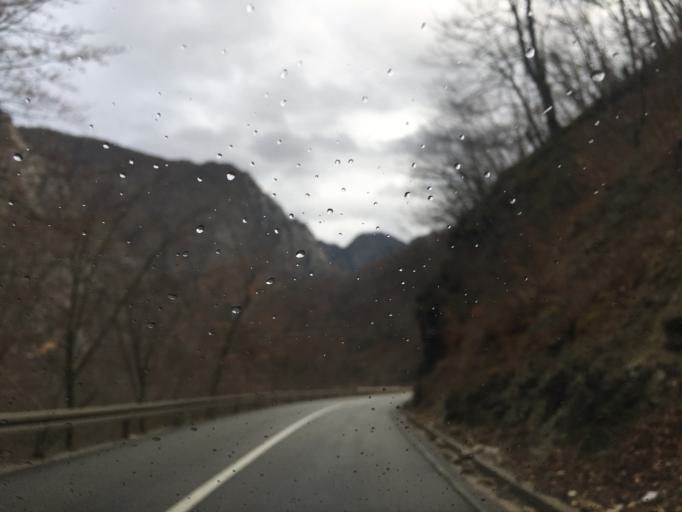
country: RS
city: Sokolovo Brdo
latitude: 43.1978
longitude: 19.7639
